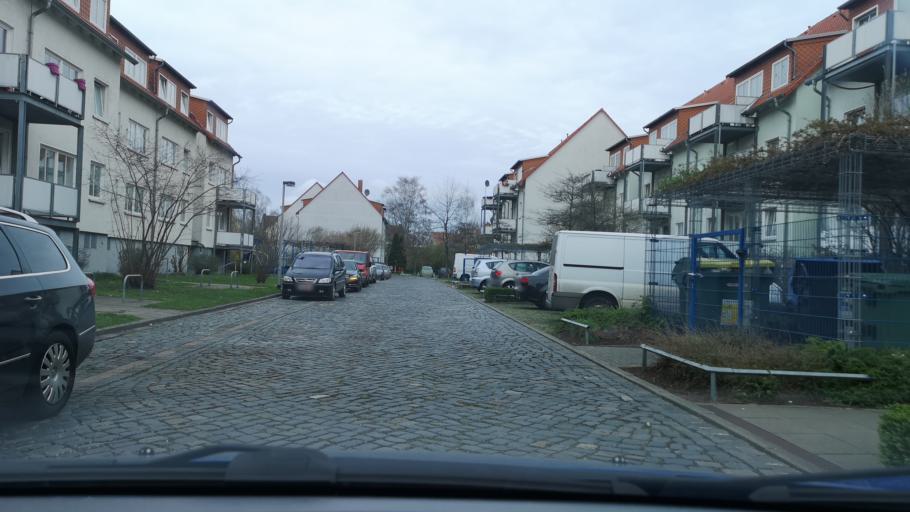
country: DE
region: Lower Saxony
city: Langenhagen
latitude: 52.4170
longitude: 9.6920
